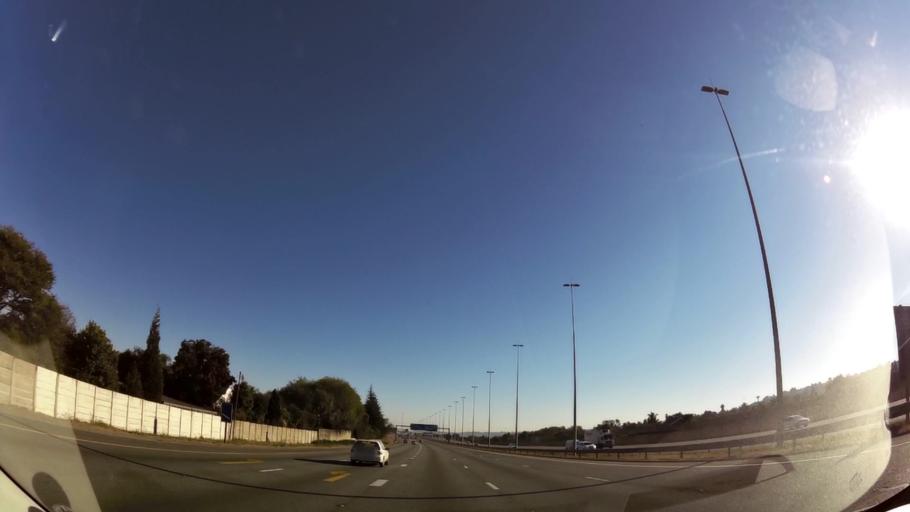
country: ZA
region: Gauteng
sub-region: City of Tshwane Metropolitan Municipality
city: Centurion
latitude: -25.8367
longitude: 28.2473
